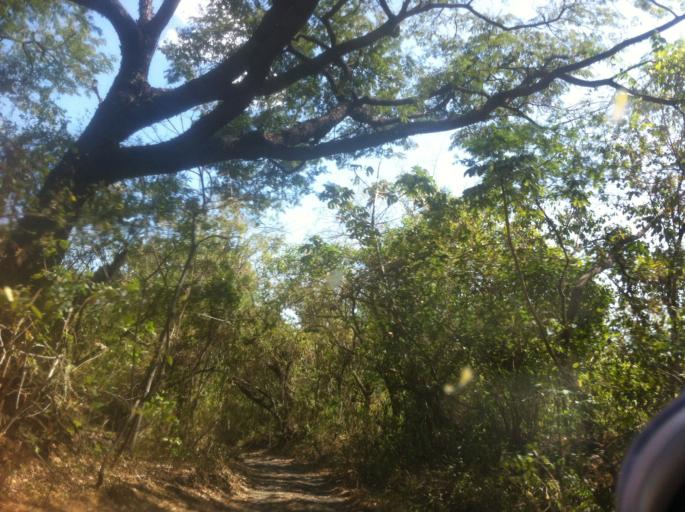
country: NI
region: Chinandega
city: Chichigalpa
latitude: 12.6853
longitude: -87.0278
